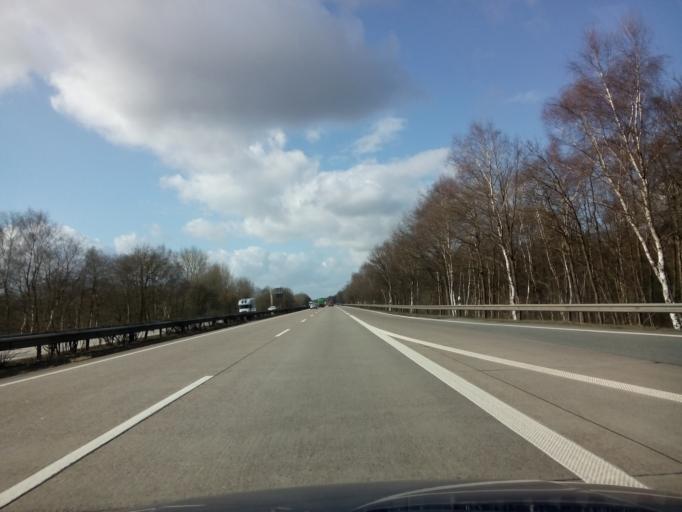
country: DE
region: Lower Saxony
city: Wildeshausen
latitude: 52.9144
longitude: 8.4201
